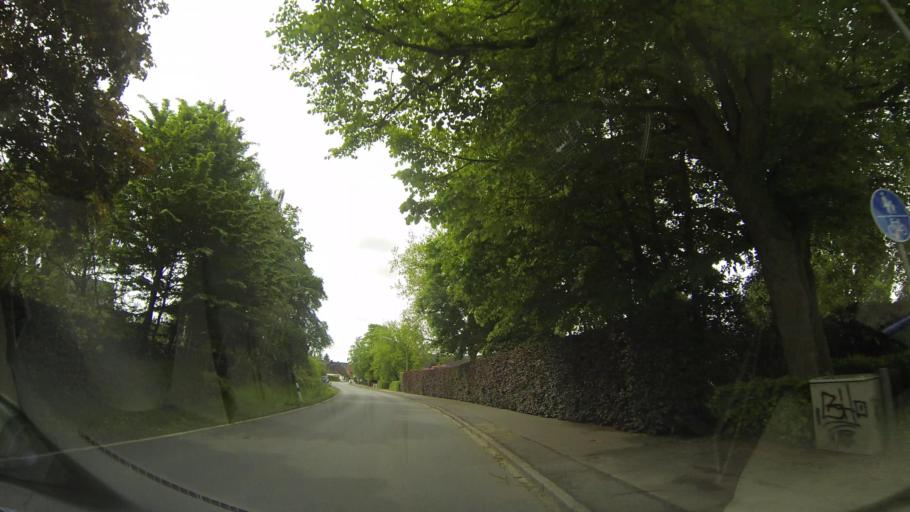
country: DE
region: Schleswig-Holstein
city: Rellingen
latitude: 53.6554
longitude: 9.8315
